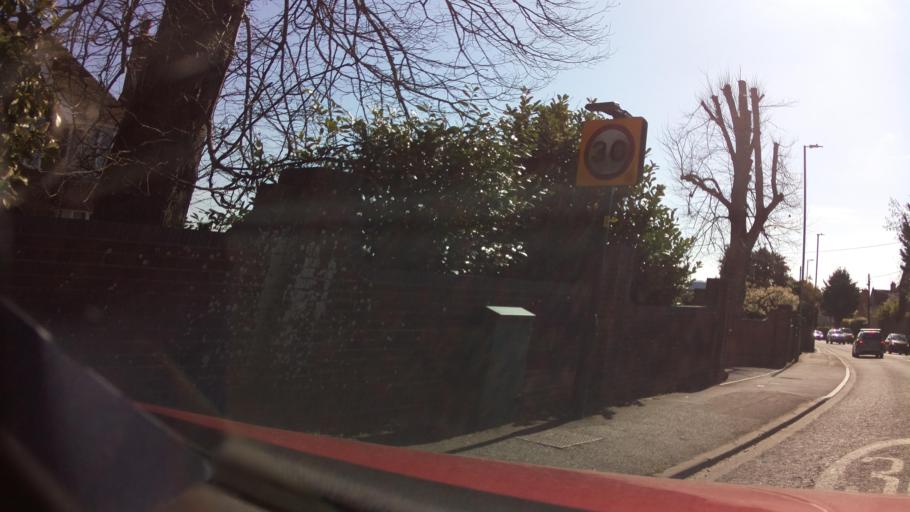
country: GB
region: England
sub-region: Wiltshire
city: Trowbridge
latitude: 51.3256
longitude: -2.2267
